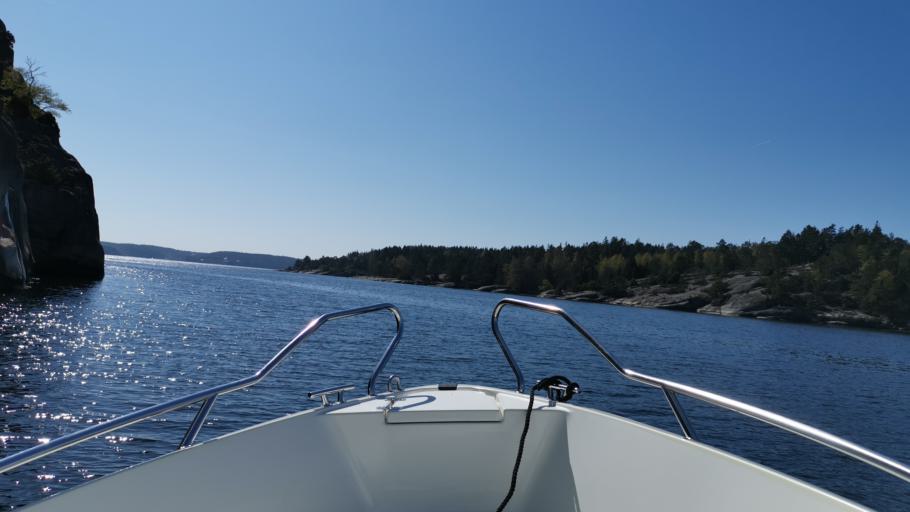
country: SE
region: Vaestra Goetaland
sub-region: Orust
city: Henan
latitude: 58.2550
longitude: 11.5740
